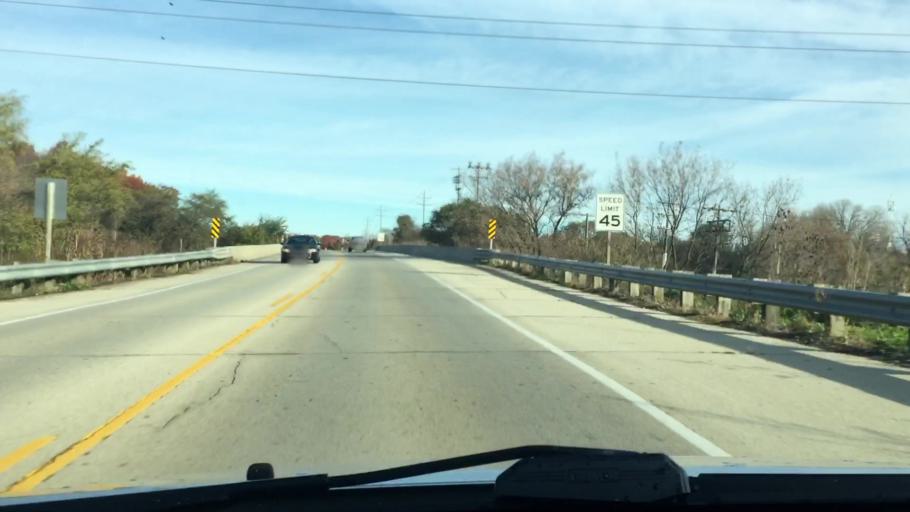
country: US
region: Wisconsin
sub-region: Waukesha County
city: Hartland
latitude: 43.0993
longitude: -88.3620
